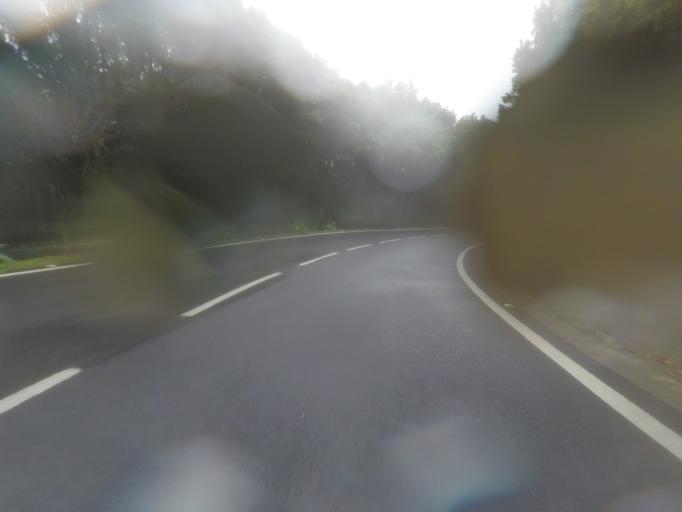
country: ES
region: Canary Islands
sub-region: Provincia de Santa Cruz de Tenerife
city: Vallehermosa
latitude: 28.1418
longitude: -17.2850
